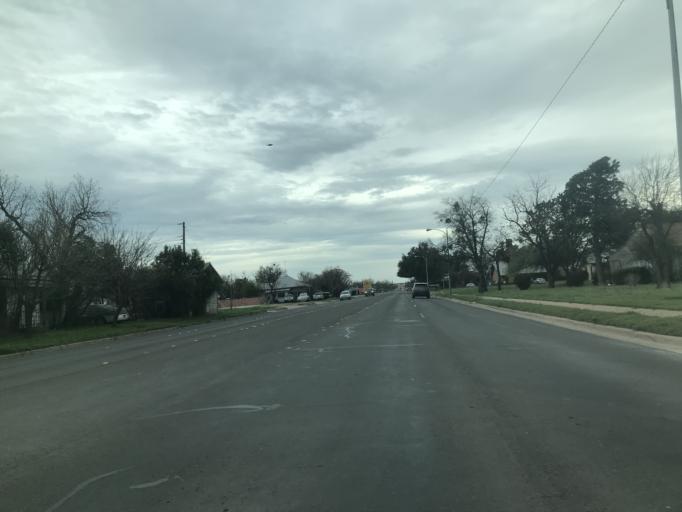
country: US
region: Texas
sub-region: Taylor County
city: Abilene
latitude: 32.4671
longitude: -99.7398
